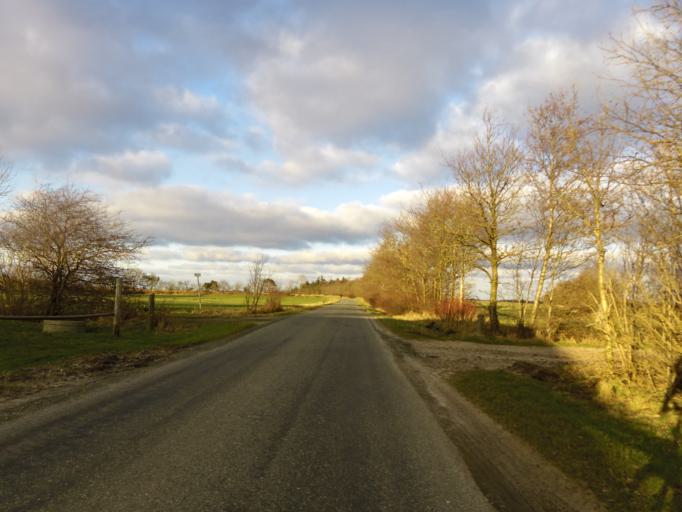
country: DK
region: South Denmark
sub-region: Esbjerg Kommune
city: Ribe
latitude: 55.2941
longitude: 8.8481
